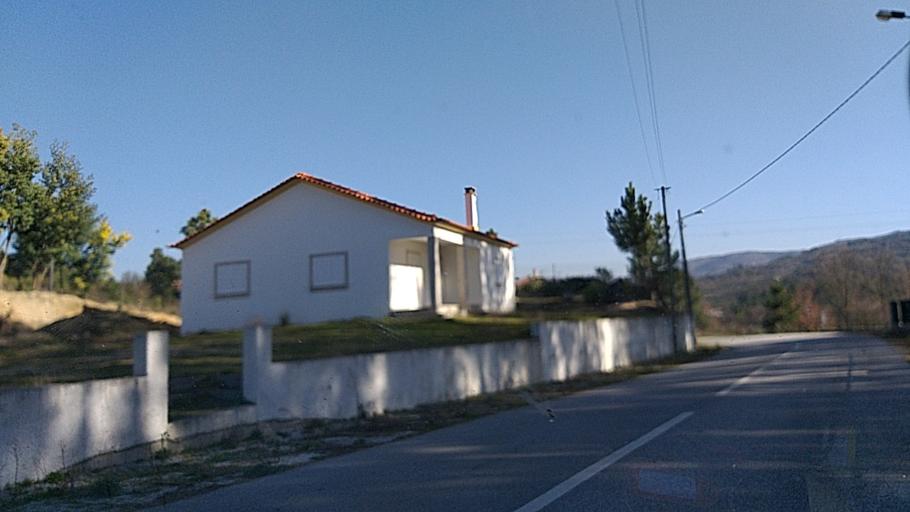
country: PT
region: Guarda
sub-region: Fornos de Algodres
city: Fornos de Algodres
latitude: 40.6485
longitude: -7.4682
